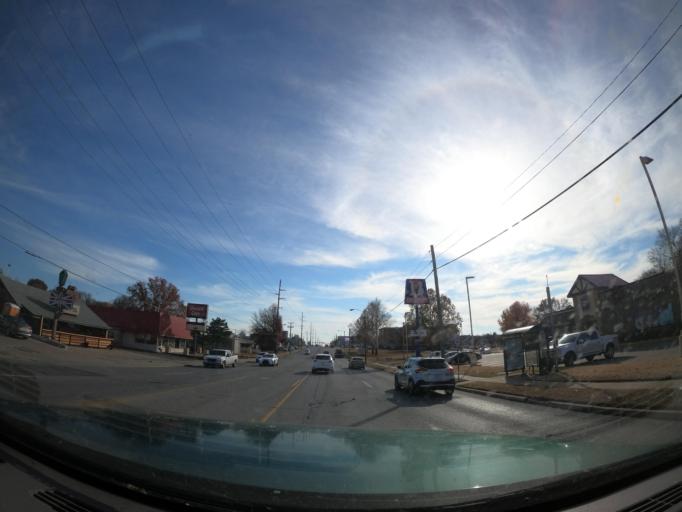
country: US
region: Oklahoma
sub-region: Tulsa County
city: Tulsa
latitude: 36.1222
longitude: -95.9403
